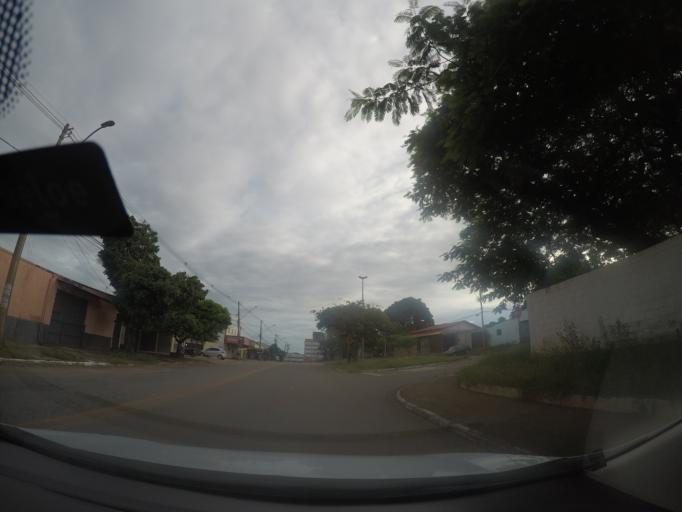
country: BR
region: Goias
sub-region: Goiania
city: Goiania
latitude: -16.6629
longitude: -49.3180
